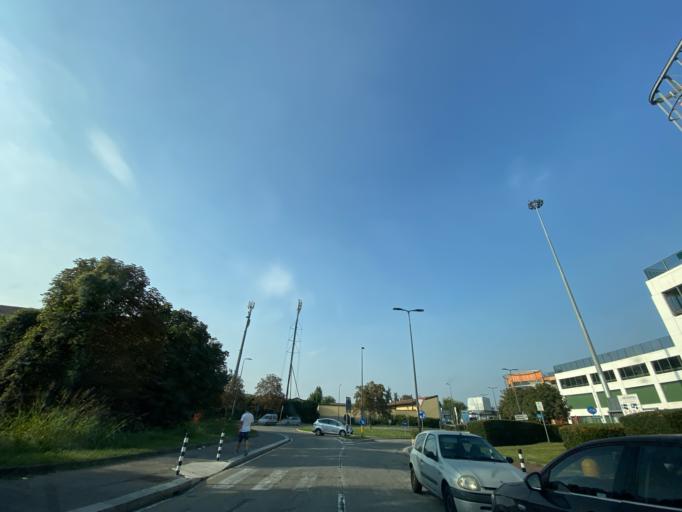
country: IT
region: Lombardy
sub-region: Citta metropolitana di Milano
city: Novate Milanese
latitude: 45.5196
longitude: 9.1482
